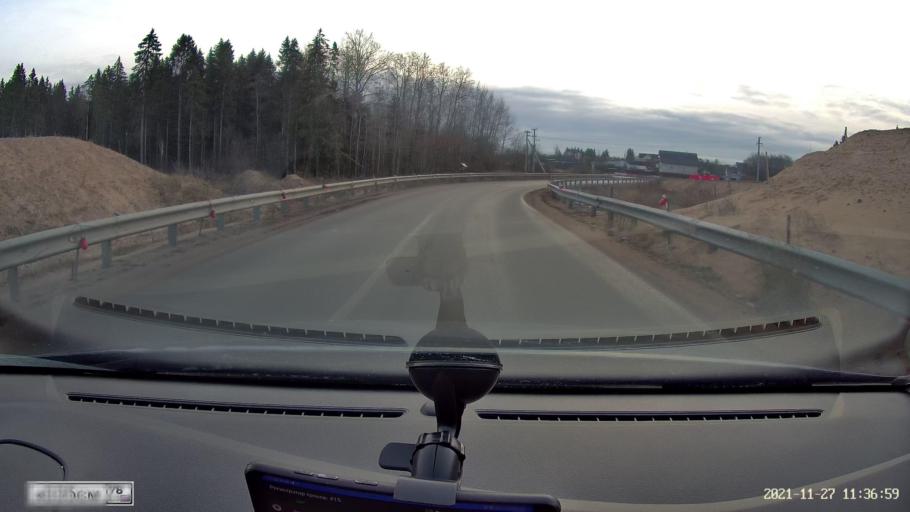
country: RU
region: Leningrad
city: Russko-Vysotskoye
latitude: 59.6964
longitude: 29.9831
